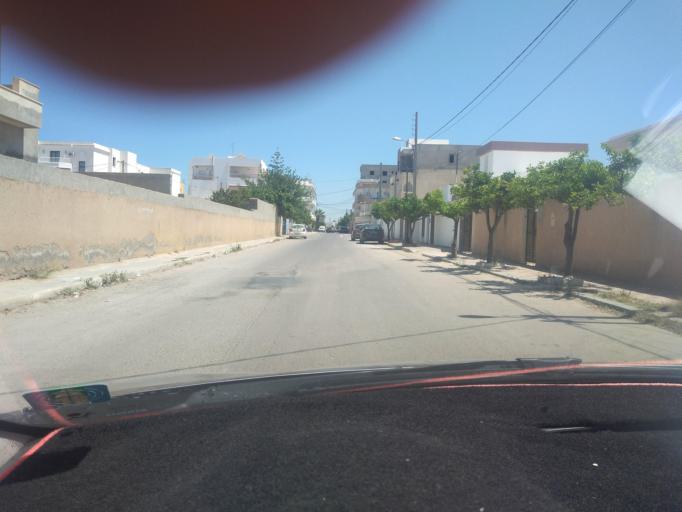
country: TN
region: Susah
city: Hammam Sousse
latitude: 35.8504
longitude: 10.5924
